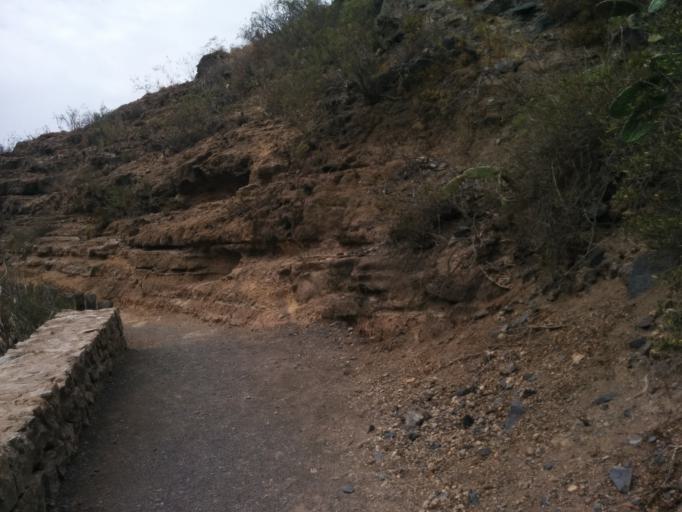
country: ES
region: Canary Islands
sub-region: Provincia de Santa Cruz de Tenerife
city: Adeje
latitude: 28.1289
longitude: -16.7203
